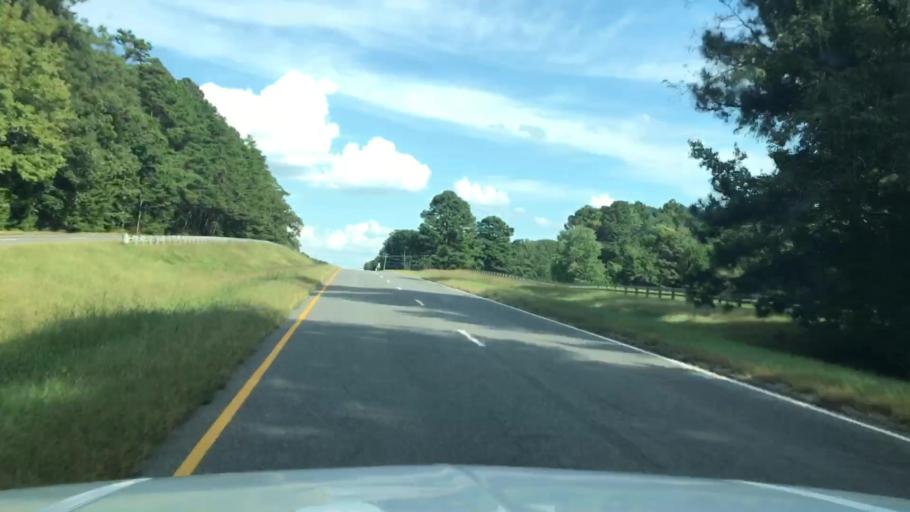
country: US
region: Virginia
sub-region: Henrico County
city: Short Pump
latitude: 37.6010
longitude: -77.6890
